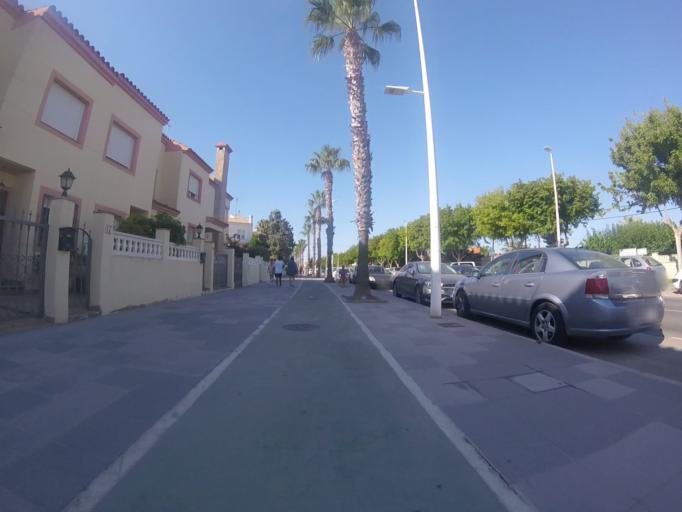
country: ES
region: Valencia
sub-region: Provincia de Castello
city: Benicarlo
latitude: 40.4030
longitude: 0.4188
